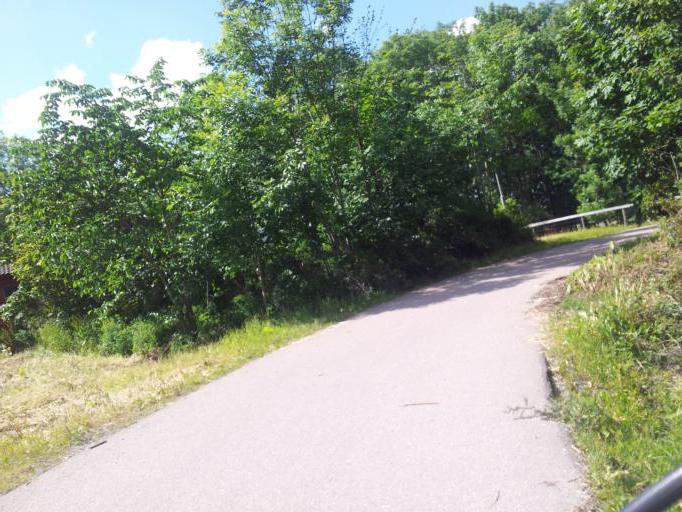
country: SE
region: Uppsala
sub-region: Uppsala Kommun
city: Uppsala
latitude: 59.8788
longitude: 17.6716
